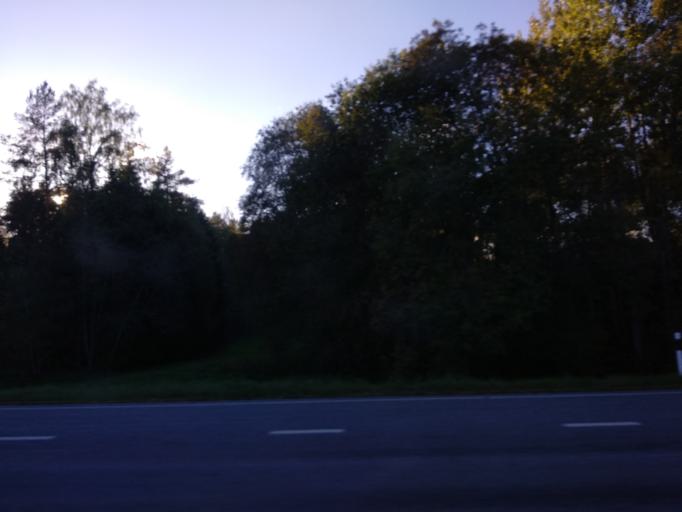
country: EE
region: Polvamaa
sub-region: Polva linn
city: Polva
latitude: 58.0431
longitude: 27.0658
